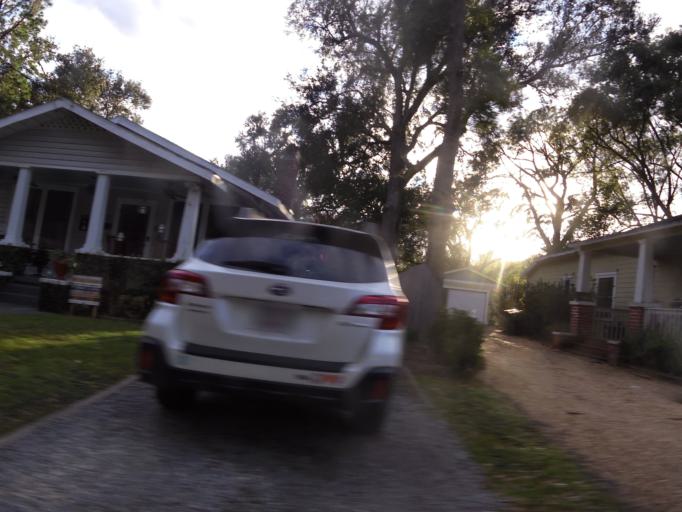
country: US
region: Florida
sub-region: Duval County
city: Jacksonville
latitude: 30.3002
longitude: -81.7123
